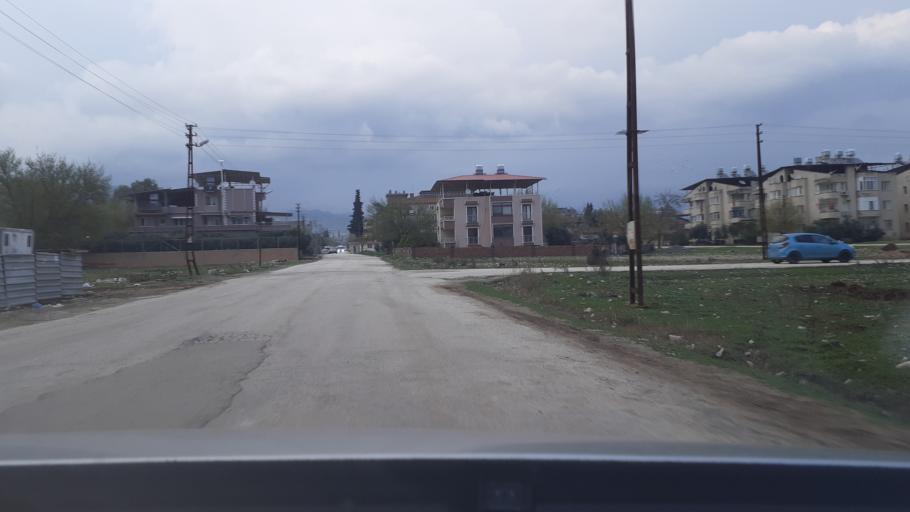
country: TR
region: Hatay
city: Kirikhan
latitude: 36.4850
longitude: 36.3556
